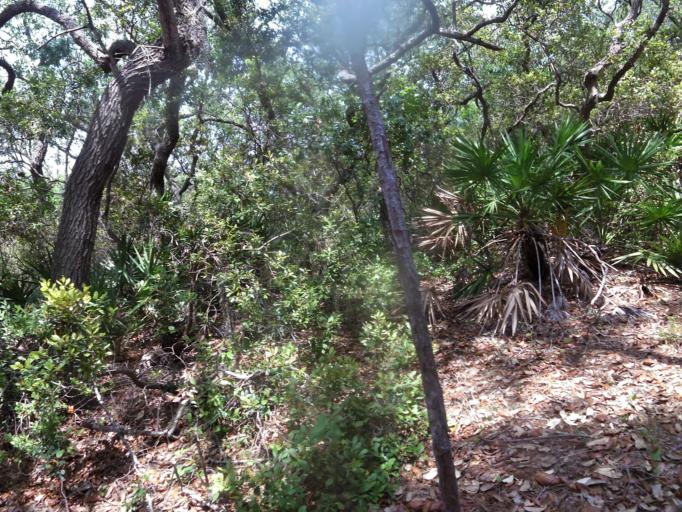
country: US
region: Florida
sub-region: Nassau County
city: Fernandina Beach
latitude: 30.4962
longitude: -81.4922
